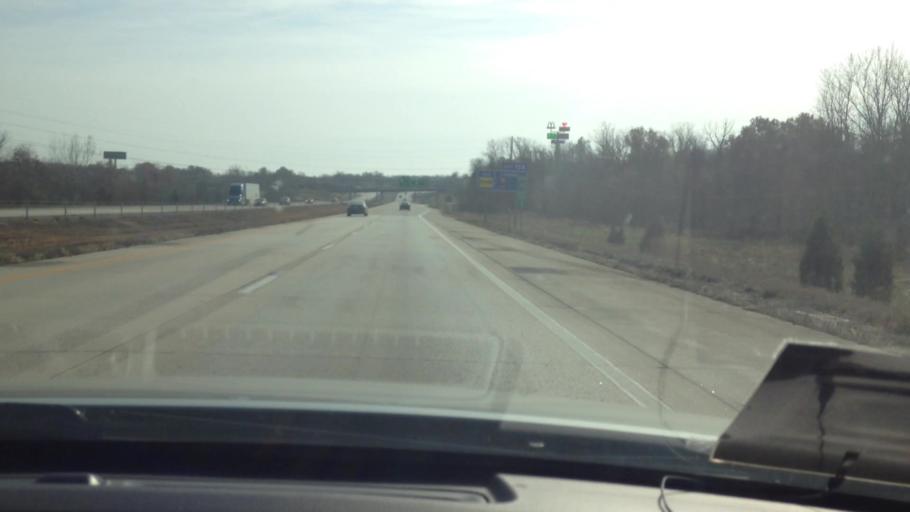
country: US
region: Missouri
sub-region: Cass County
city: Harrisonville
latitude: 38.6413
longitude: -94.3583
